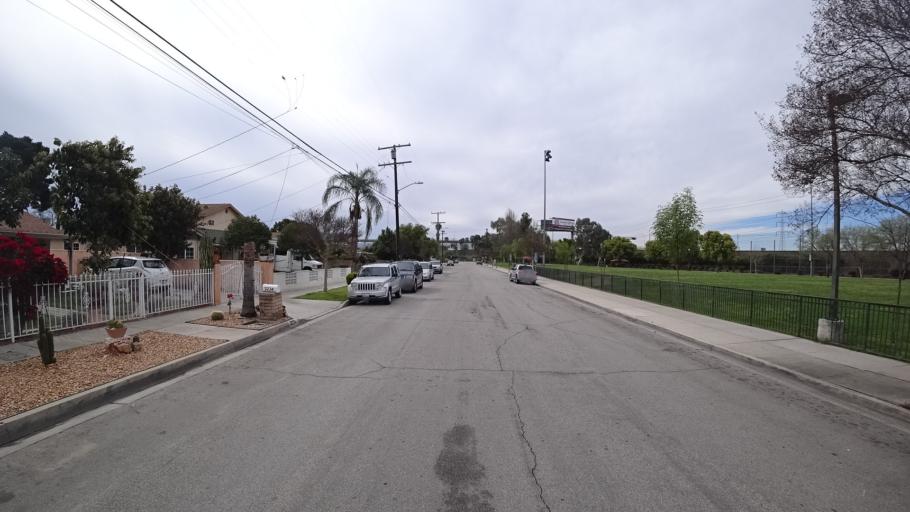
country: US
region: California
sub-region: Los Angeles County
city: El Monte
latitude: 34.0696
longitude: -117.9992
